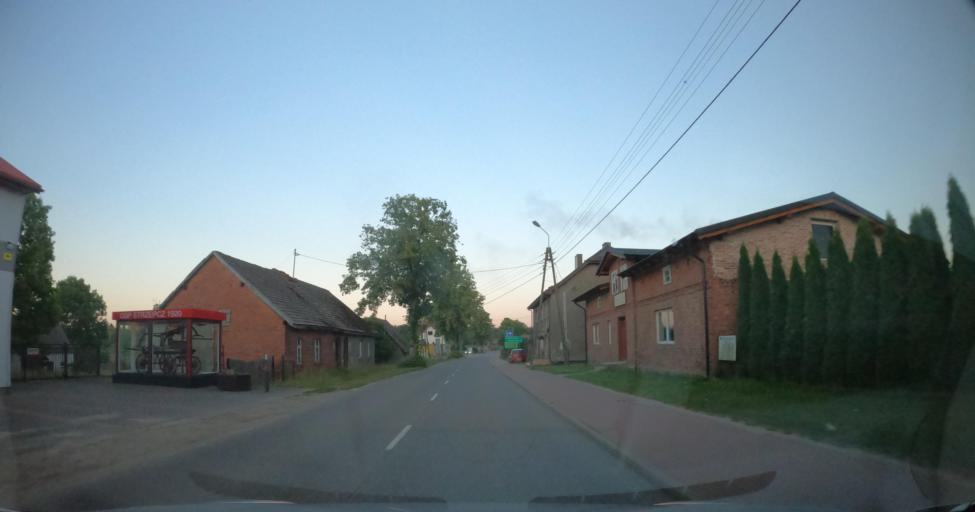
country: PL
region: Pomeranian Voivodeship
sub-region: Powiat wejherowski
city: Linia
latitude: 54.4551
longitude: 18.0267
